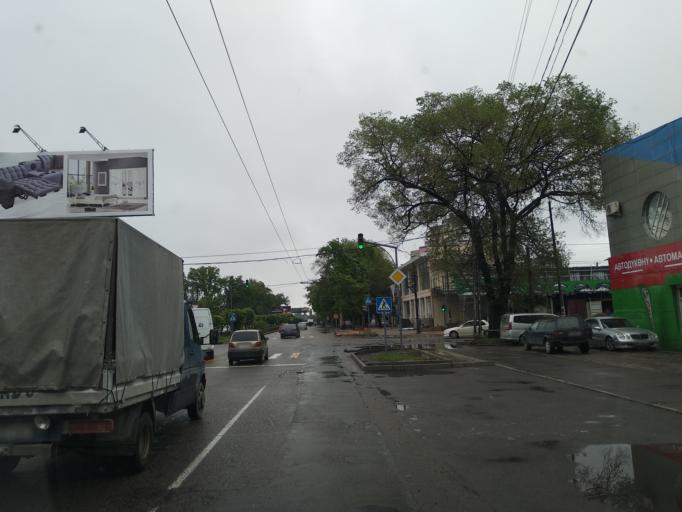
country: KG
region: Chuy
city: Bishkek
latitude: 42.8857
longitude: 74.6220
